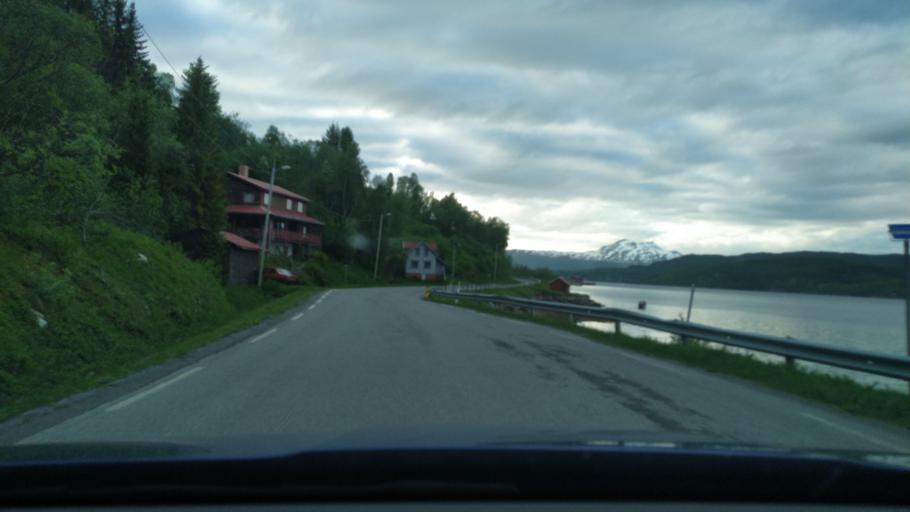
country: NO
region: Troms
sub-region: Sorreisa
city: Sorreisa
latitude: 69.1395
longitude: 18.0579
